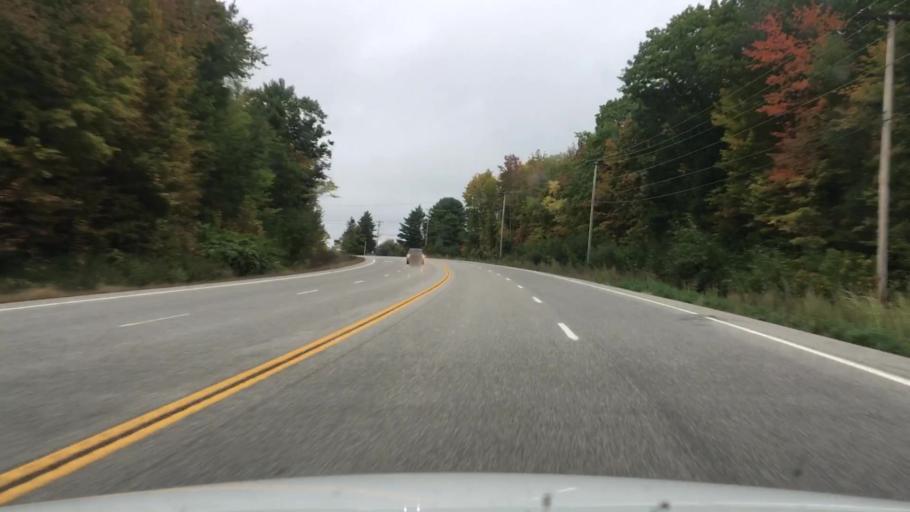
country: US
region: Maine
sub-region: Androscoggin County
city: Poland
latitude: 44.0215
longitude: -70.3639
